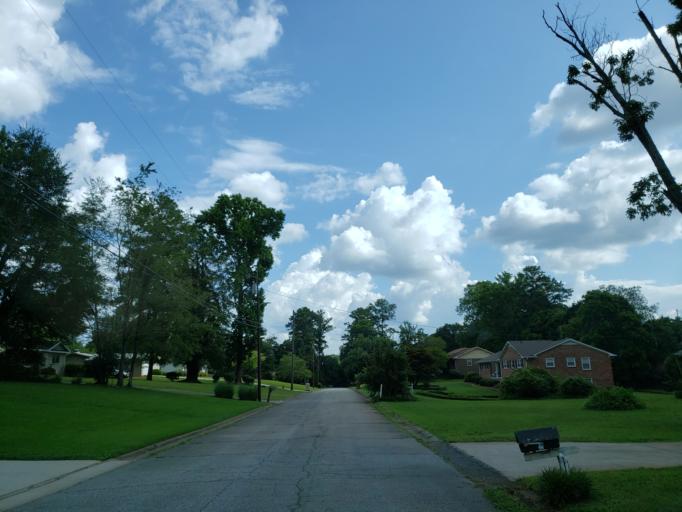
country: US
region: Georgia
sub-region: Cobb County
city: Marietta
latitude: 33.9779
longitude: -84.4637
